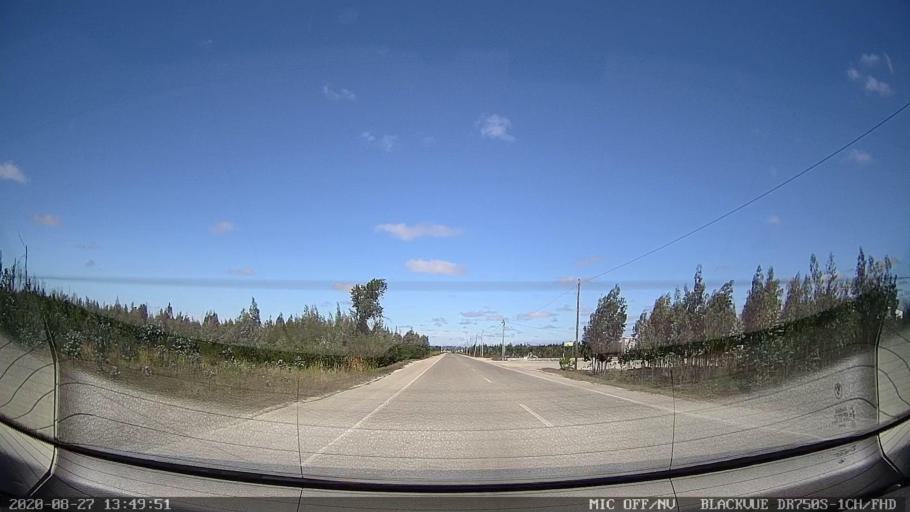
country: PT
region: Coimbra
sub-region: Mira
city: Mira
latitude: 40.3631
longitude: -8.7468
